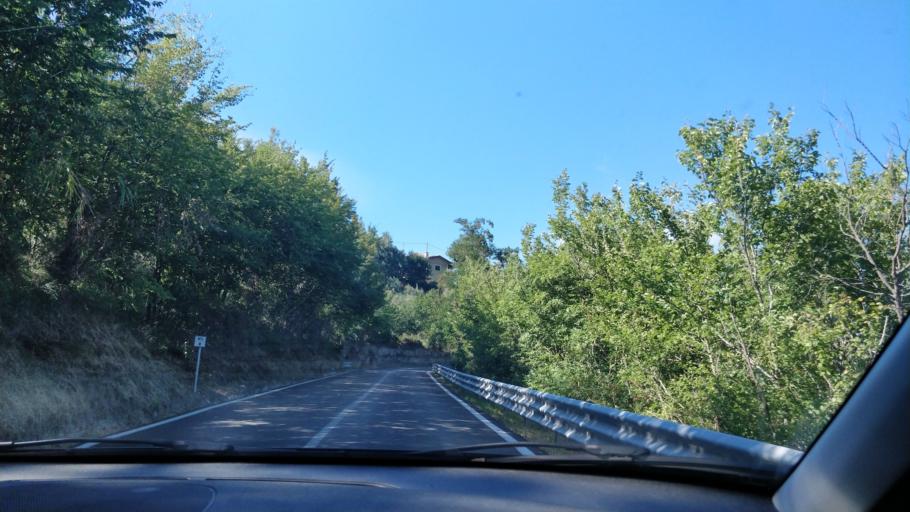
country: IT
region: Abruzzo
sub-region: Provincia di Pescara
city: Serramonacesca
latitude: 42.2532
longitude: 14.0896
